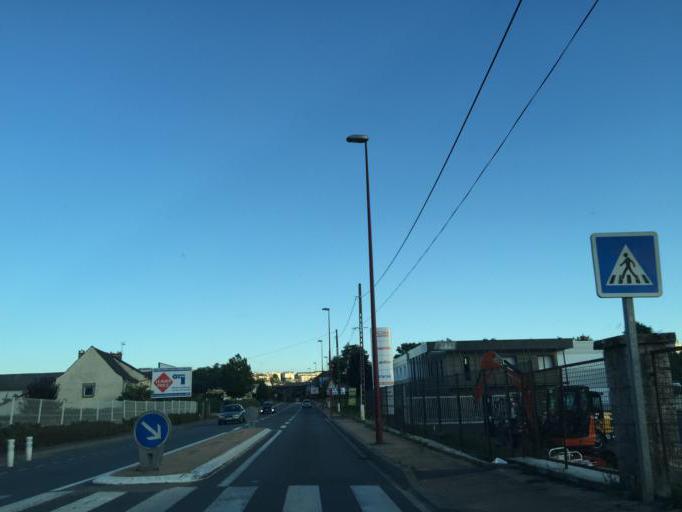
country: FR
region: Midi-Pyrenees
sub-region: Departement de l'Aveyron
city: Rodez
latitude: 44.3681
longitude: 2.5712
